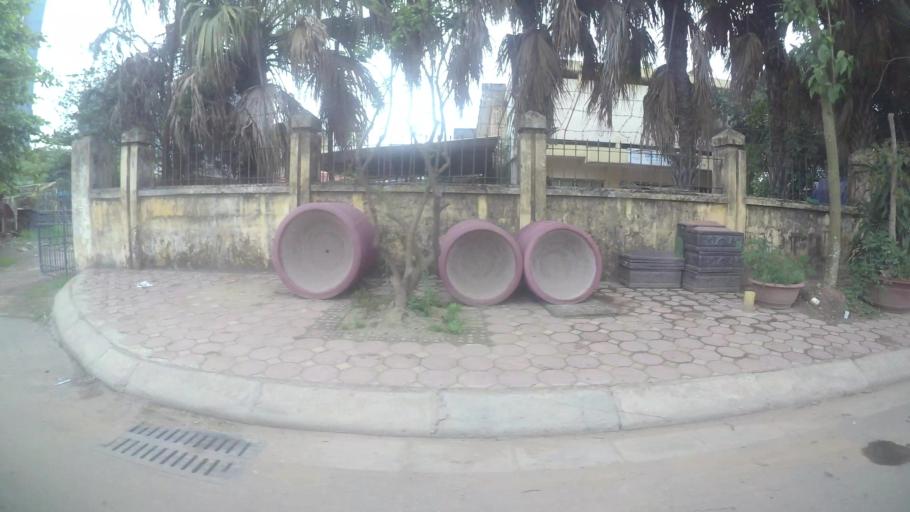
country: VN
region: Ha Noi
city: Tay Ho
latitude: 21.0883
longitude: 105.7920
